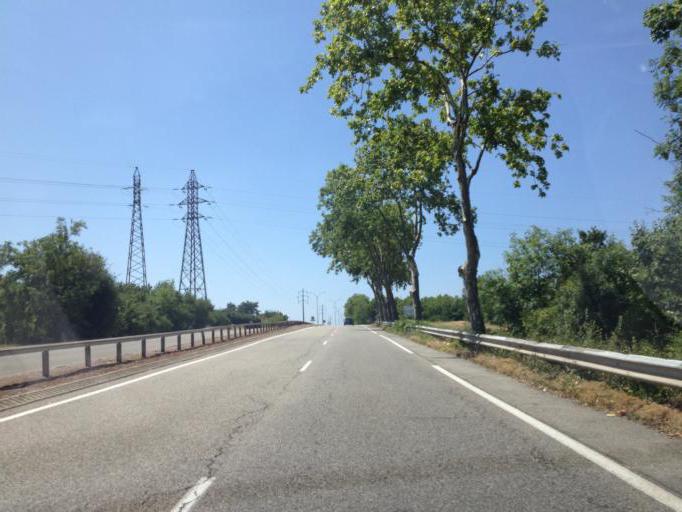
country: FR
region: Rhone-Alpes
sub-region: Departement de la Drome
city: Bourg-les-Valence
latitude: 44.9476
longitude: 4.9244
